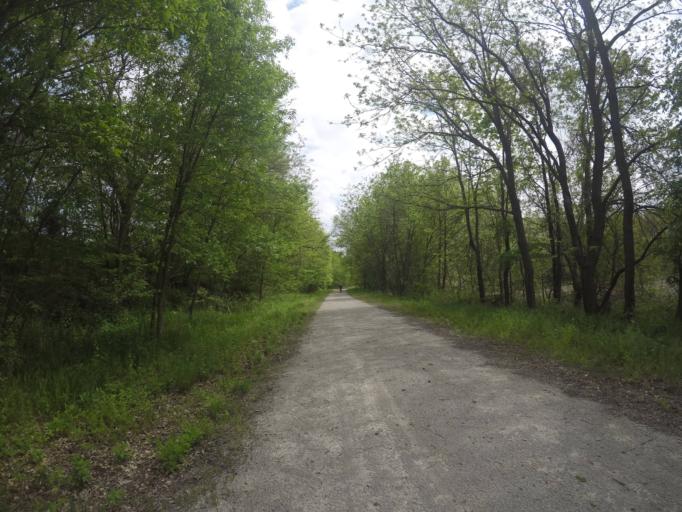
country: US
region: Kansas
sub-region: Marshall County
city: Marysville
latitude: 39.9755
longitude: -96.6003
